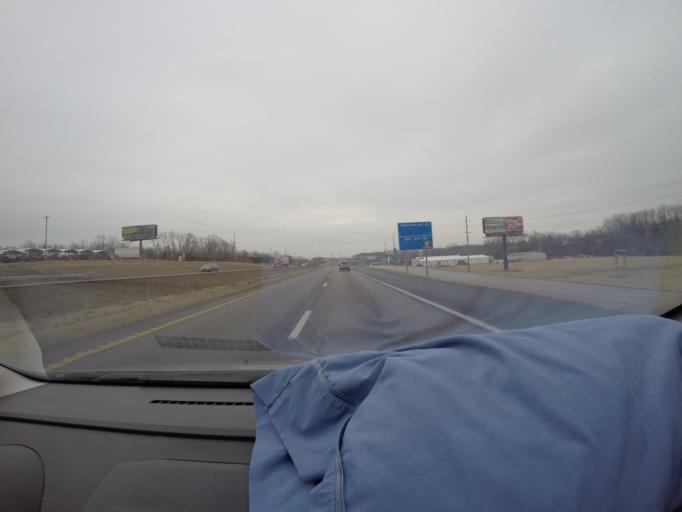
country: US
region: Missouri
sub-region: Warren County
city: Warrenton
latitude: 38.8203
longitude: -91.1585
